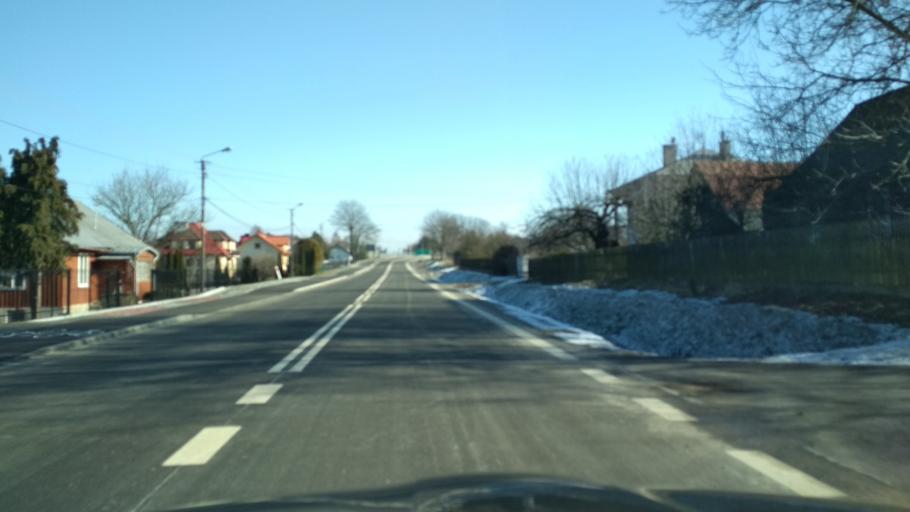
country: PL
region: Subcarpathian Voivodeship
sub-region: Powiat ropczycko-sedziszowski
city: Sedziszow Malopolski
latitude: 50.0699
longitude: 21.7375
